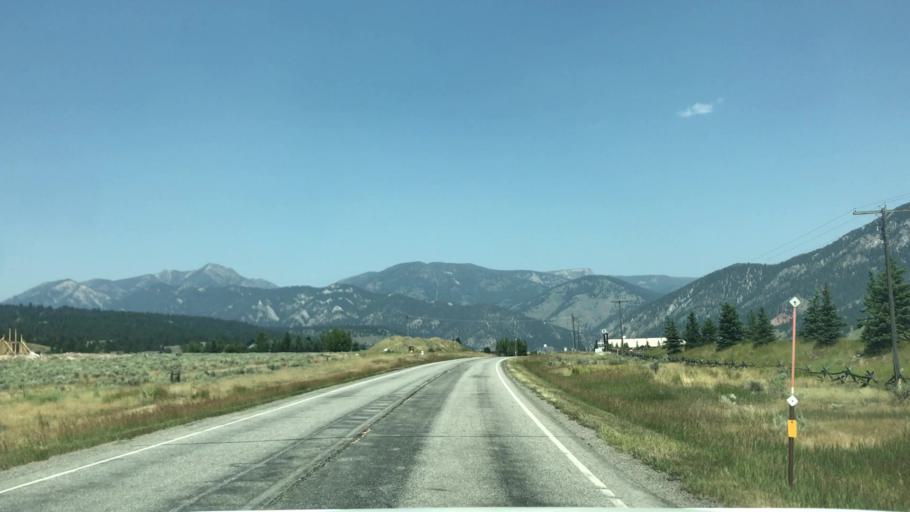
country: US
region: Montana
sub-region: Gallatin County
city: Big Sky
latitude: 45.2208
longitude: -111.2505
